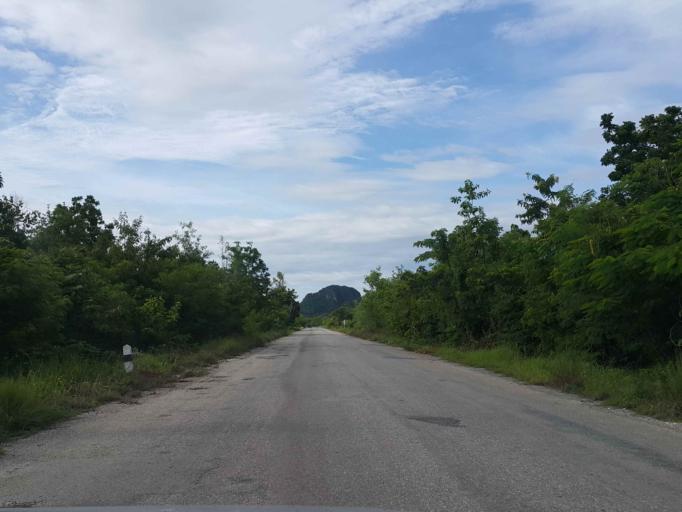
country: TH
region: Sukhothai
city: Thung Saliam
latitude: 17.3011
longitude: 99.5271
